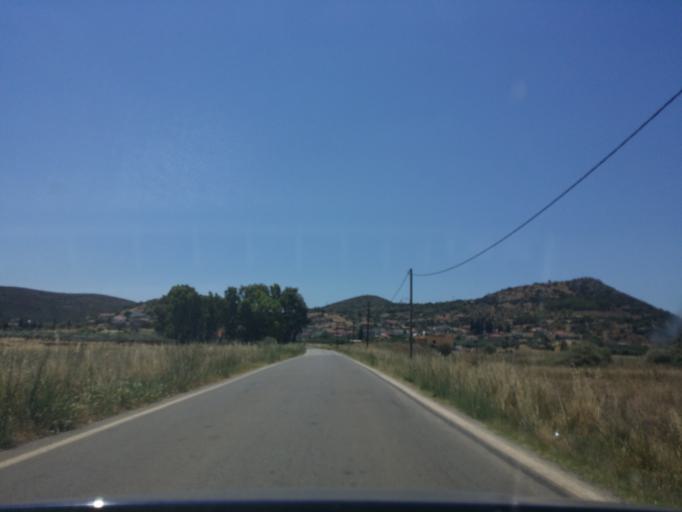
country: GR
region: Peloponnese
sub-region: Nomos Lakonias
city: Kato Glikovrisi
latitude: 36.8889
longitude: 22.8006
